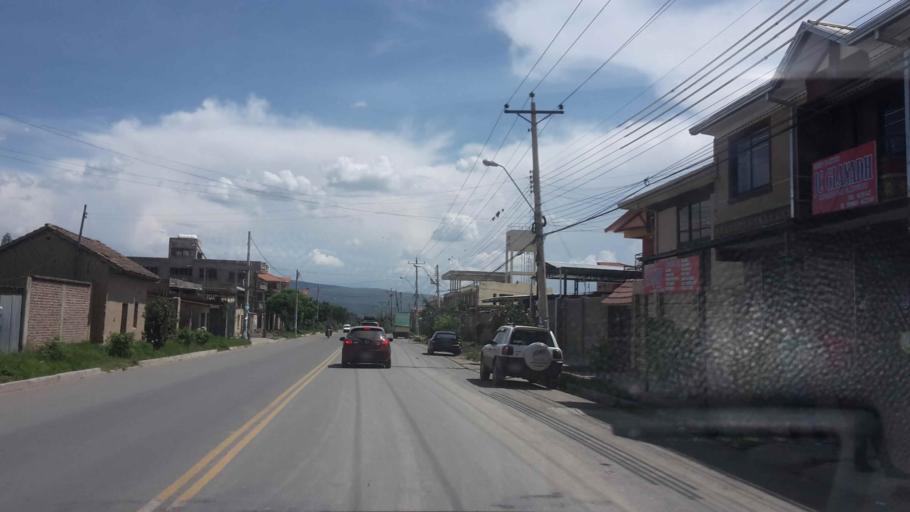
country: BO
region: Cochabamba
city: Cochabamba
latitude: -17.3646
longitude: -66.2301
